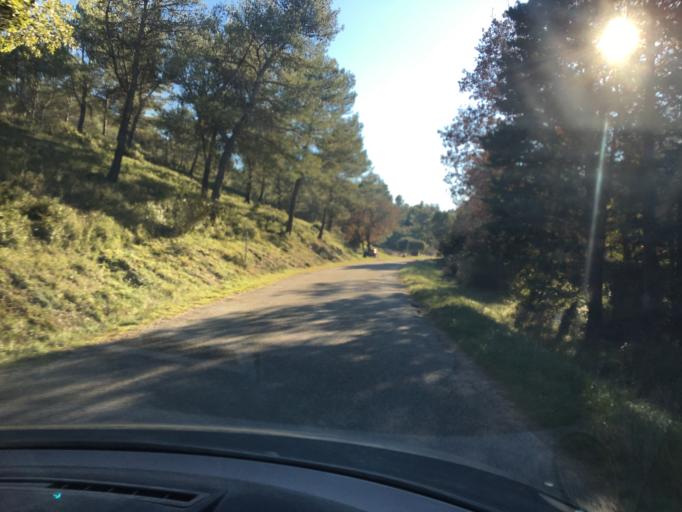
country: FR
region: Provence-Alpes-Cote d'Azur
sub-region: Departement des Bouches-du-Rhone
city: Saint-Remy-de-Provence
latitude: 43.7723
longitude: 4.7940
